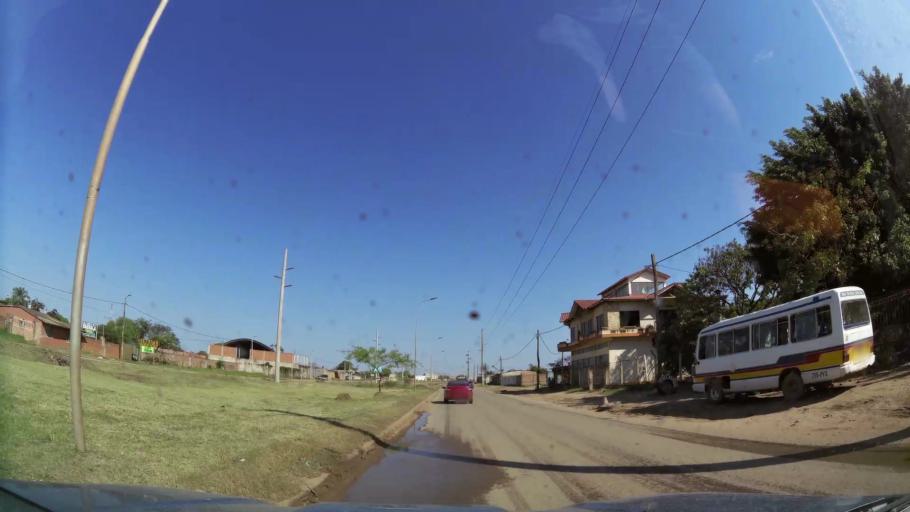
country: BO
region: Santa Cruz
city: Cotoca
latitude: -17.7752
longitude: -63.1077
